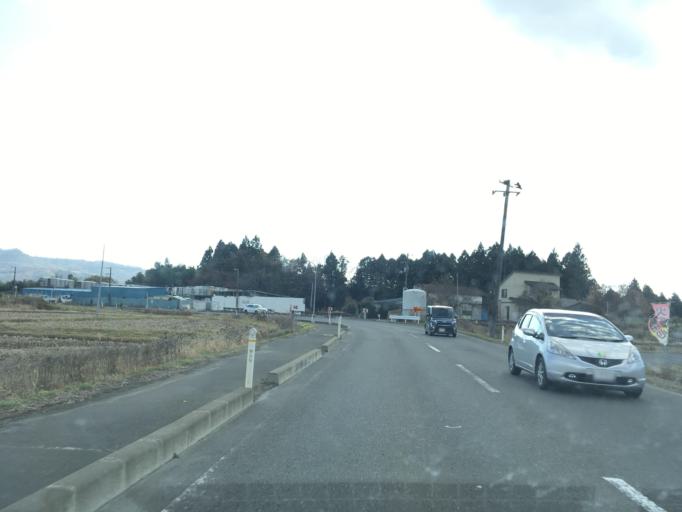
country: JP
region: Miyagi
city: Sendai
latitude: 38.2820
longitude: 140.7568
